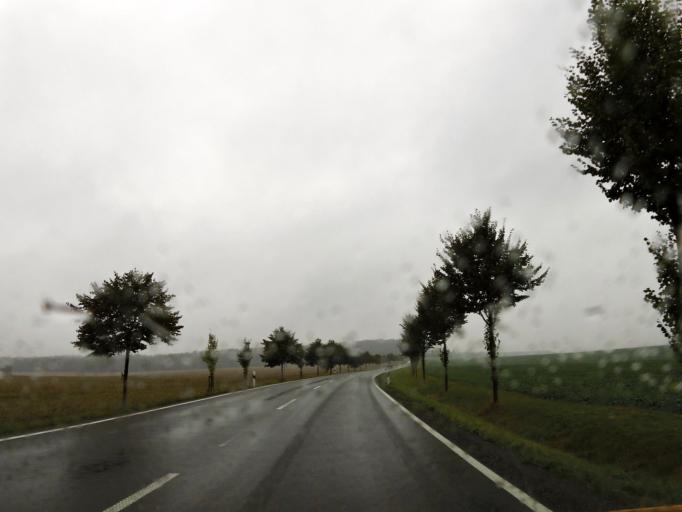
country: DE
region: Saxony-Anhalt
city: Friedrichsbrunn
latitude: 51.6457
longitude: 11.0381
